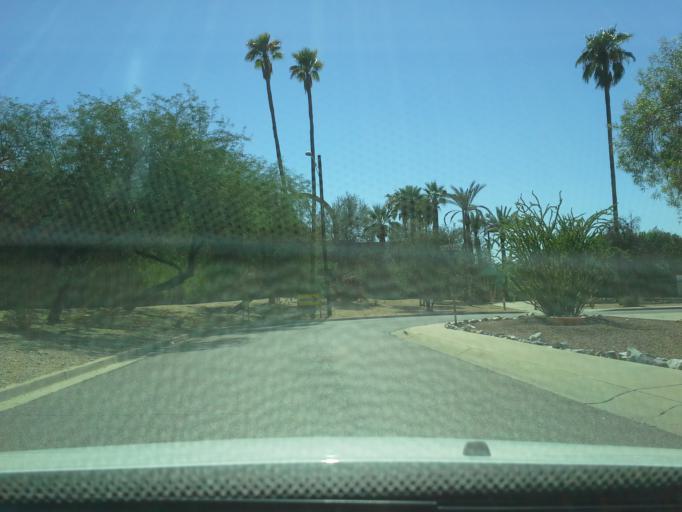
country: US
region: Arizona
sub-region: Maricopa County
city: Phoenix
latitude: 33.5337
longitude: -112.0423
